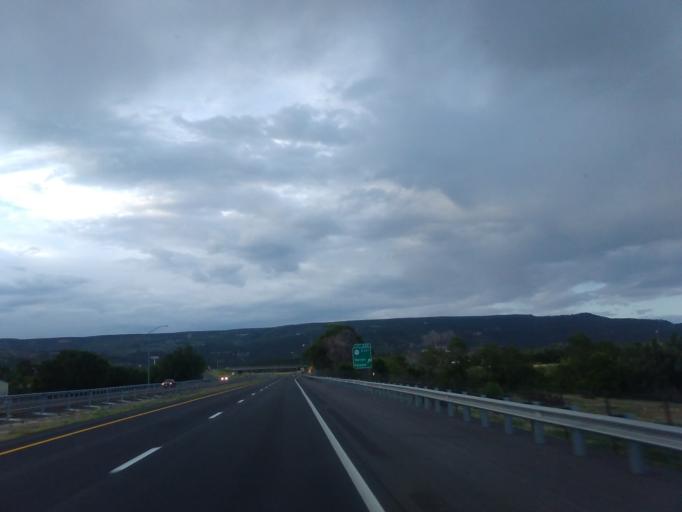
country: US
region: New Mexico
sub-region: Colfax County
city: Raton
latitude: 36.8959
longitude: -104.4265
